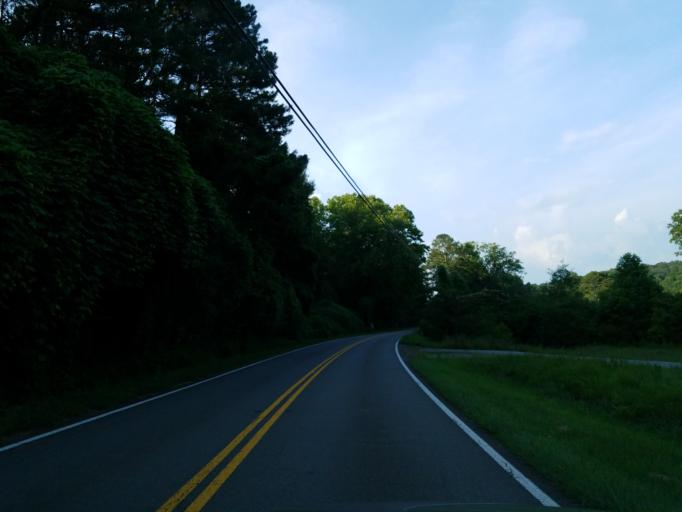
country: US
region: Georgia
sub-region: Gilmer County
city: Ellijay
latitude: 34.5917
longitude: -84.5324
